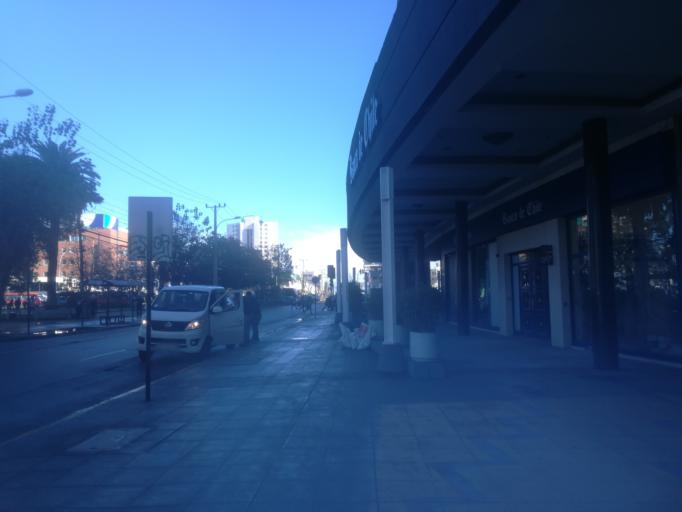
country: CL
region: Valparaiso
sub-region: Provincia de Valparaiso
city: Vina del Mar
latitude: -33.0093
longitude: -71.5476
